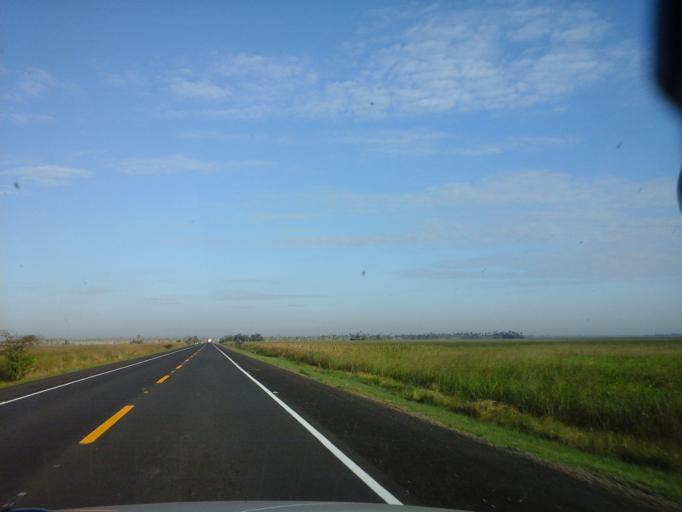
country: PY
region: Neembucu
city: Cerrito
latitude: -26.8932
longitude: -57.7097
